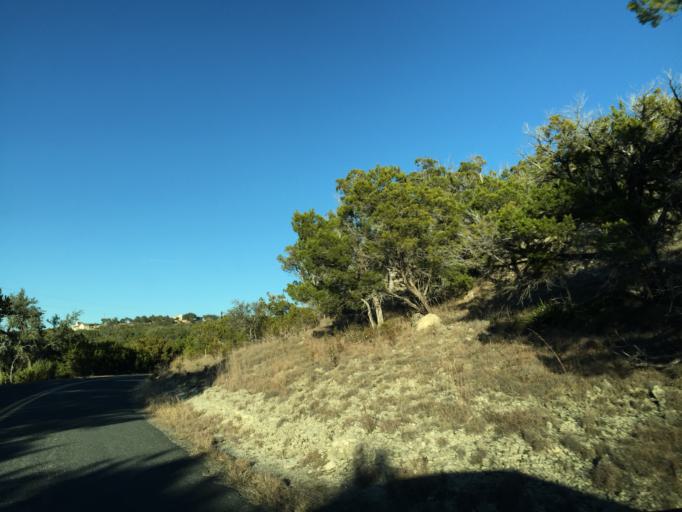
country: US
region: Texas
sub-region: Travis County
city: Briarcliff
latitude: 30.5147
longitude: -98.0995
